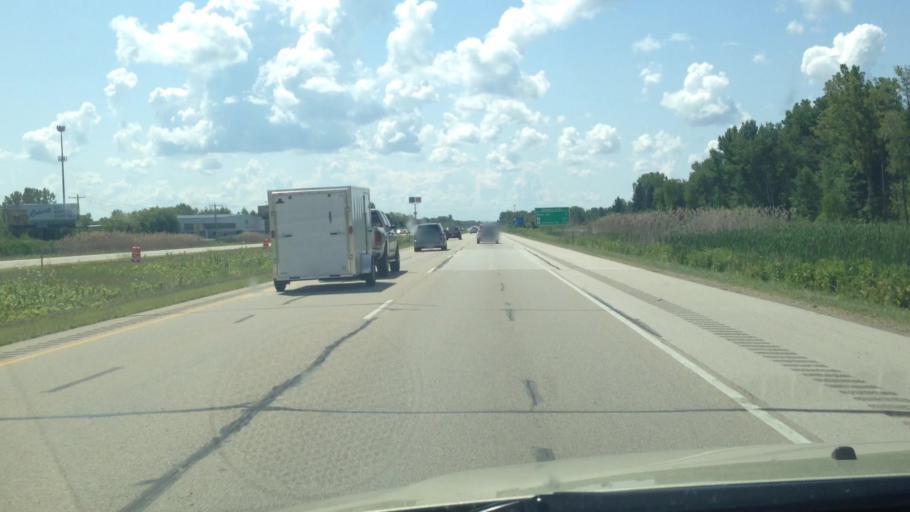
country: US
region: Wisconsin
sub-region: Brown County
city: Suamico
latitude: 44.6886
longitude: -88.0506
